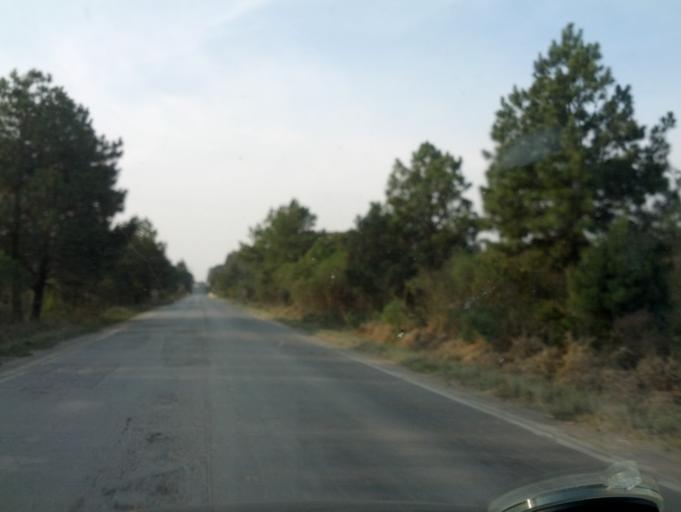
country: BR
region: Santa Catarina
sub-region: Otacilio Costa
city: Otacilio Costa
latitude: -27.5180
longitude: -50.1337
